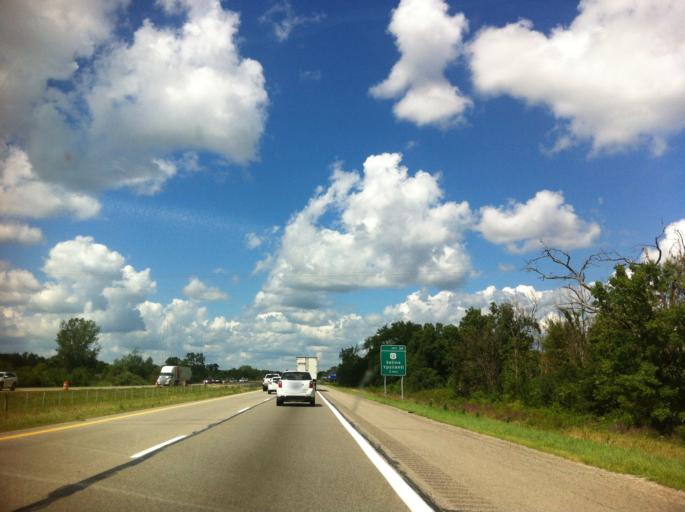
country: US
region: Michigan
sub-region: Washtenaw County
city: Ypsilanti
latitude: 42.1853
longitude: -83.6844
